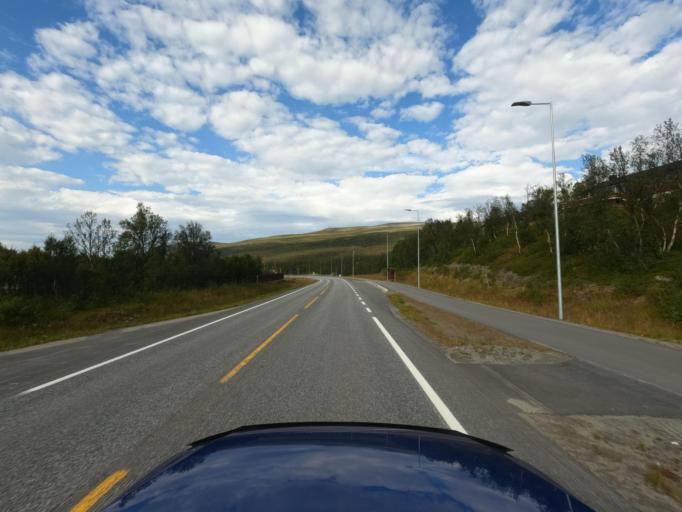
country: NO
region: Finnmark Fylke
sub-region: Kvalsund
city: Kvalsund
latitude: 70.4396
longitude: 24.4760
